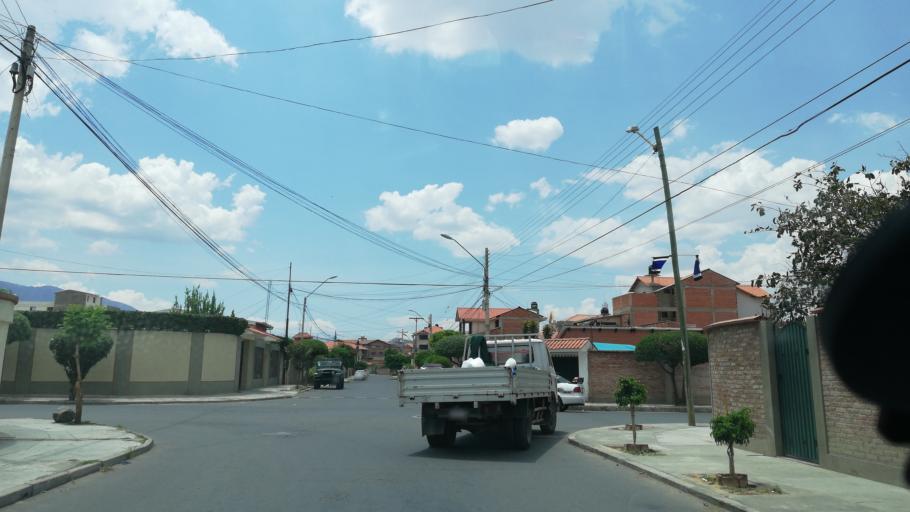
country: BO
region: Cochabamba
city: Cochabamba
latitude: -17.3781
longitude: -66.1929
